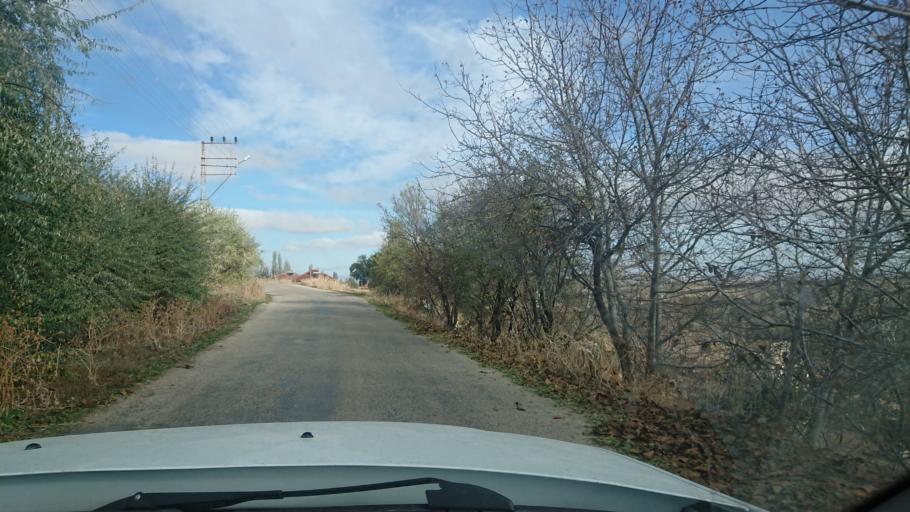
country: TR
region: Aksaray
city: Ortakoy
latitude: 38.8079
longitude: 33.9838
